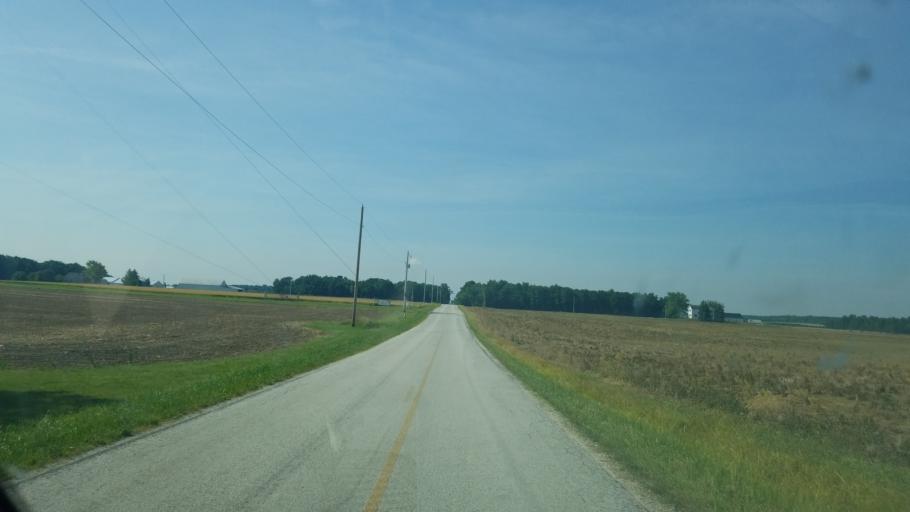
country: US
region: Ohio
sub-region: Wyandot County
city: Carey
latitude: 41.0235
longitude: -83.3629
